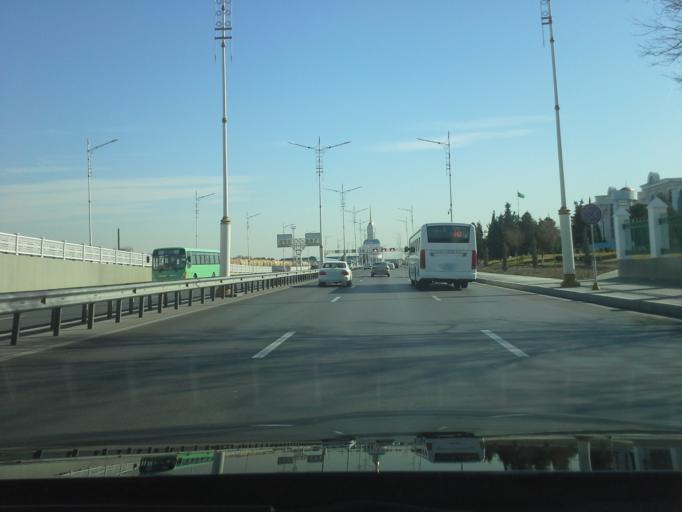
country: TM
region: Ahal
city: Ashgabat
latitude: 37.9460
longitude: 58.3898
